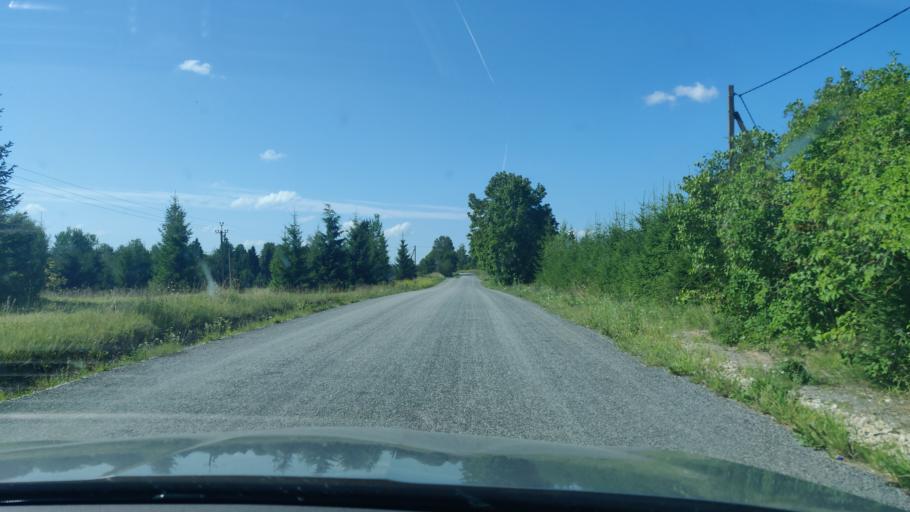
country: EE
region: Tartu
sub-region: Elva linn
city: Elva
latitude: 58.1198
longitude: 26.4662
